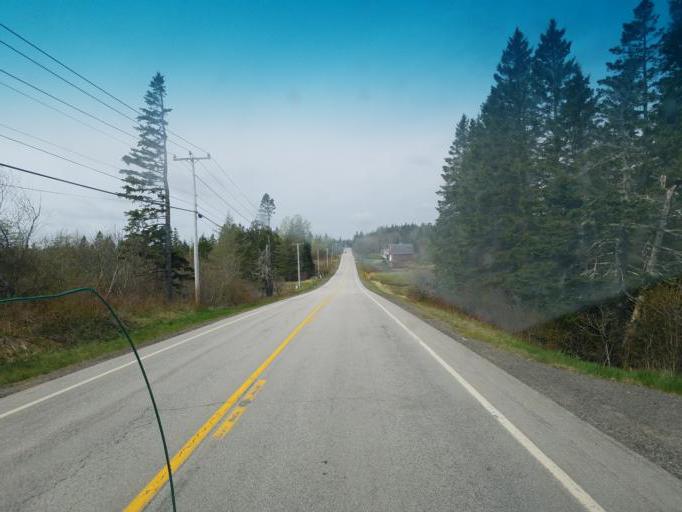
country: US
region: Maine
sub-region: Washington County
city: Eastport
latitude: 44.8025
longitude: -67.1152
